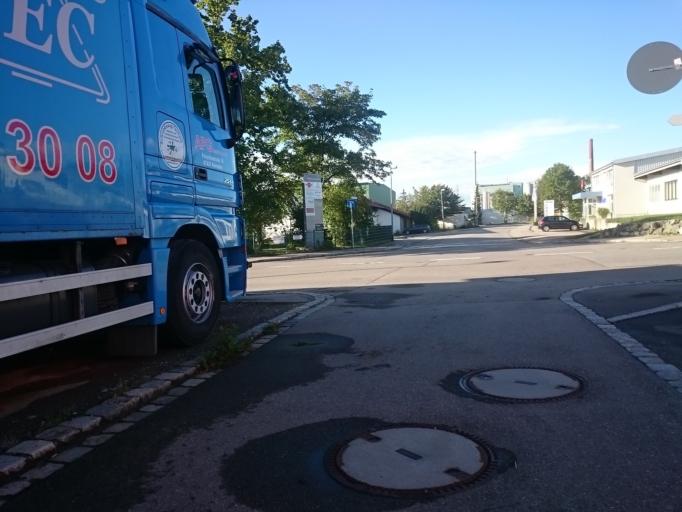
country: DE
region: Bavaria
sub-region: Swabia
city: Kempten (Allgaeu)
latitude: 47.7543
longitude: 10.3192
